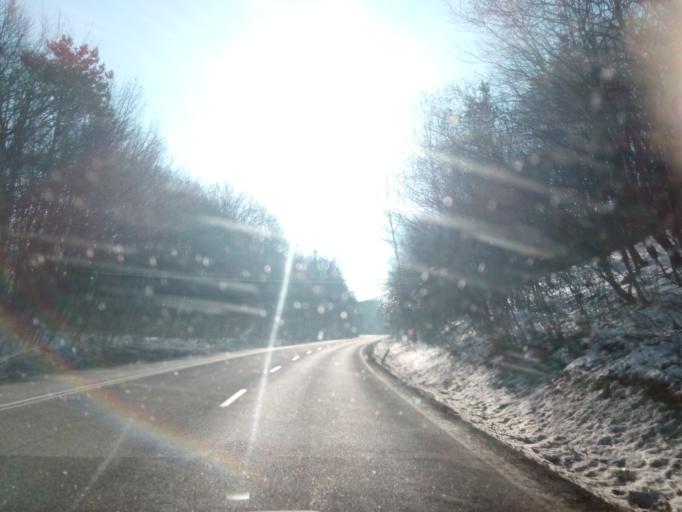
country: SK
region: Kosicky
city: Kosice
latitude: 48.7348
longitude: 21.3798
